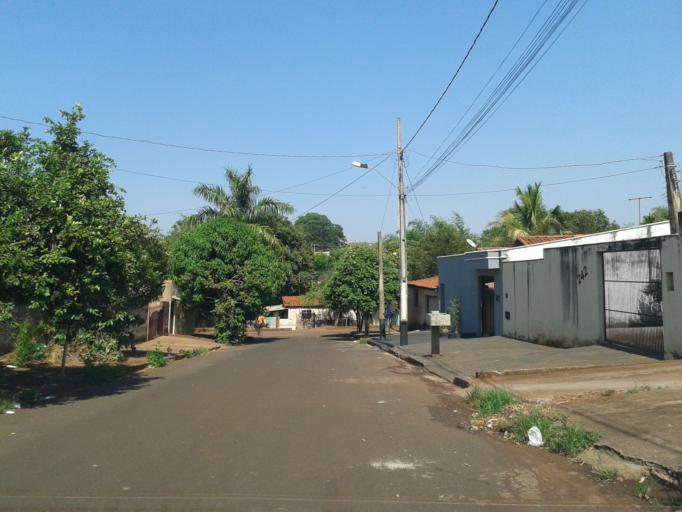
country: BR
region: Minas Gerais
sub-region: Ituiutaba
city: Ituiutaba
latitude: -18.9567
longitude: -49.4530
